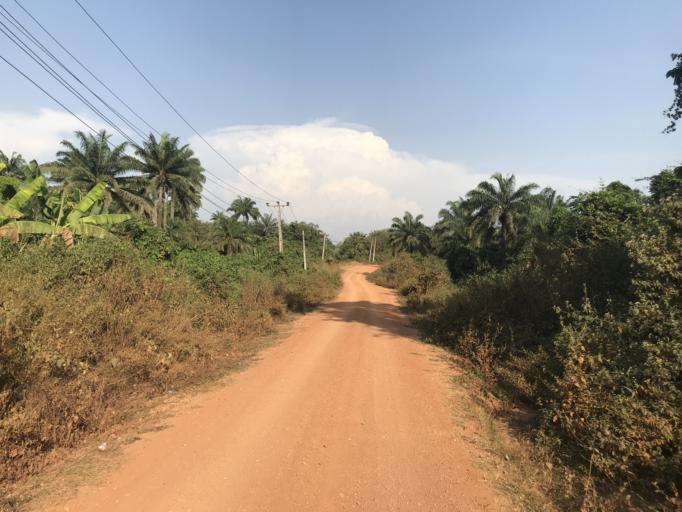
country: NG
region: Osun
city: Bode Osi
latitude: 7.7671
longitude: 4.3091
